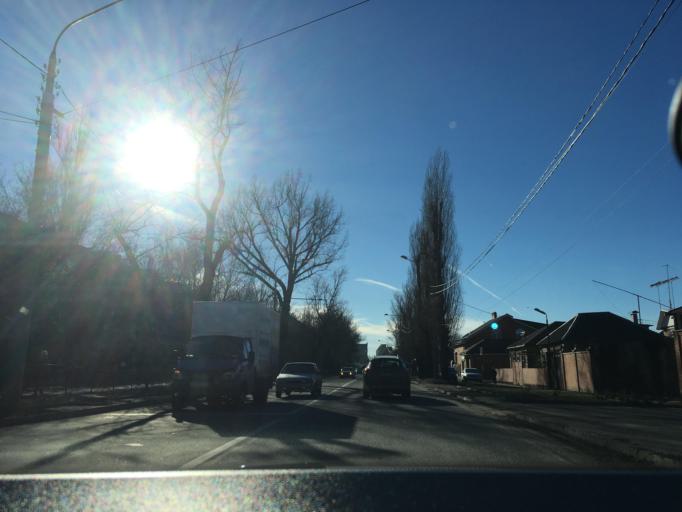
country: RU
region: Rostov
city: Imeni Chkalova
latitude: 47.2712
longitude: 39.7907
